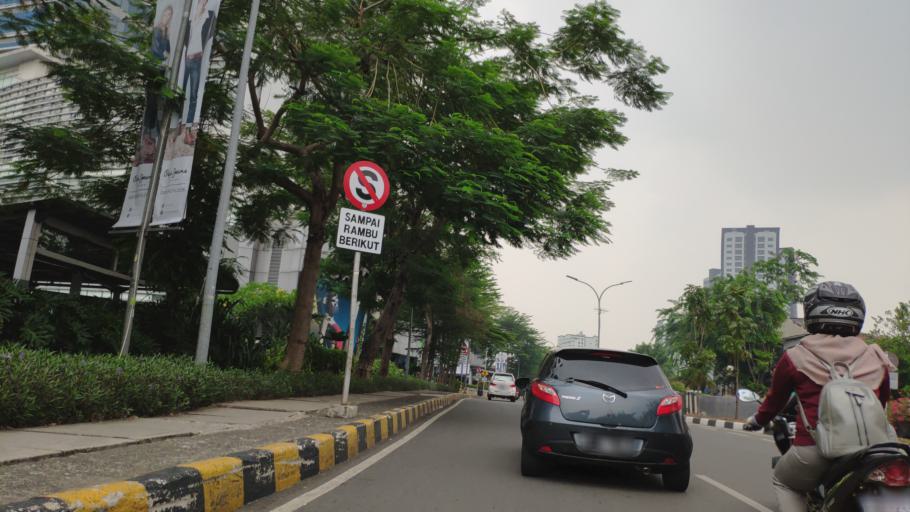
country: ID
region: Jakarta Raya
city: Jakarta
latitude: -6.2457
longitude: 106.7828
